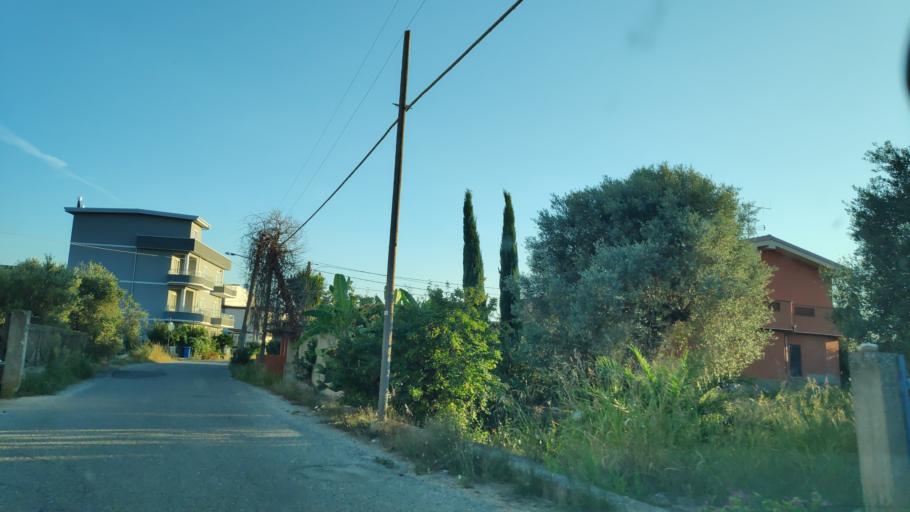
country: IT
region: Calabria
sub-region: Provincia di Reggio Calabria
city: Monasterace Marina
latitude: 38.4323
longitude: 16.5638
